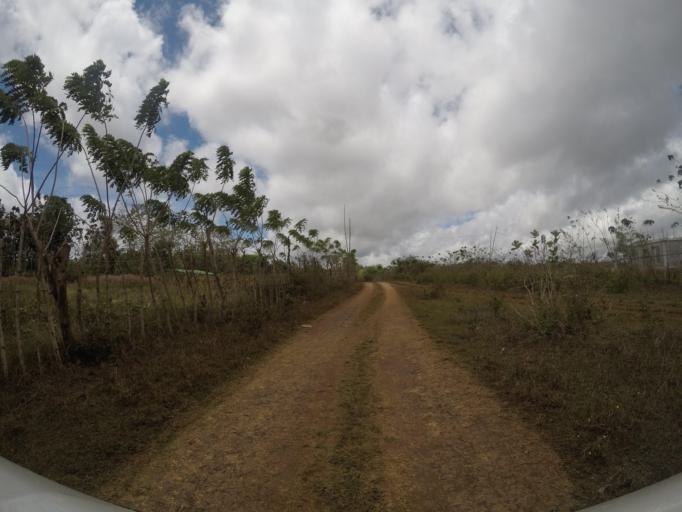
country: TL
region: Lautem
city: Lospalos
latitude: -8.4735
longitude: 126.9893
